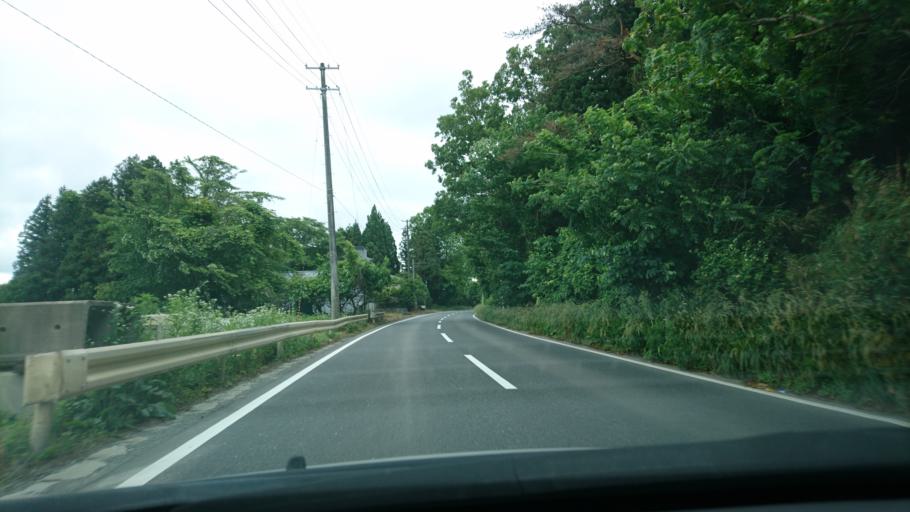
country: JP
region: Iwate
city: Ichinoseki
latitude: 38.7572
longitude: 141.2563
